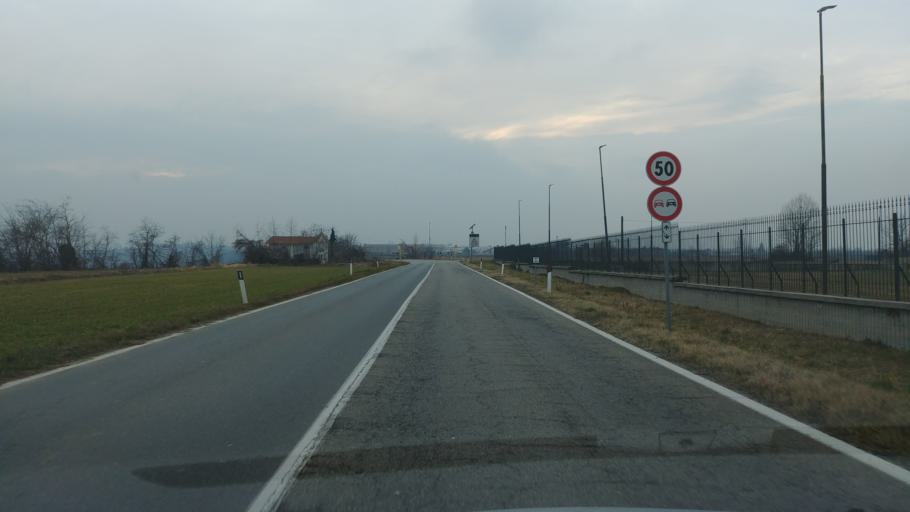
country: IT
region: Piedmont
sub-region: Provincia di Cuneo
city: Cuneo
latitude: 44.4286
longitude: 7.5748
